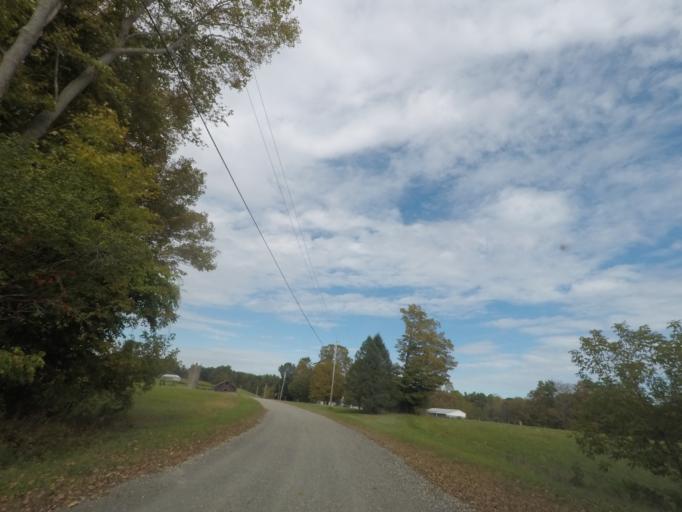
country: US
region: New York
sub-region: Rensselaer County
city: Nassau
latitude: 42.5735
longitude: -73.6181
